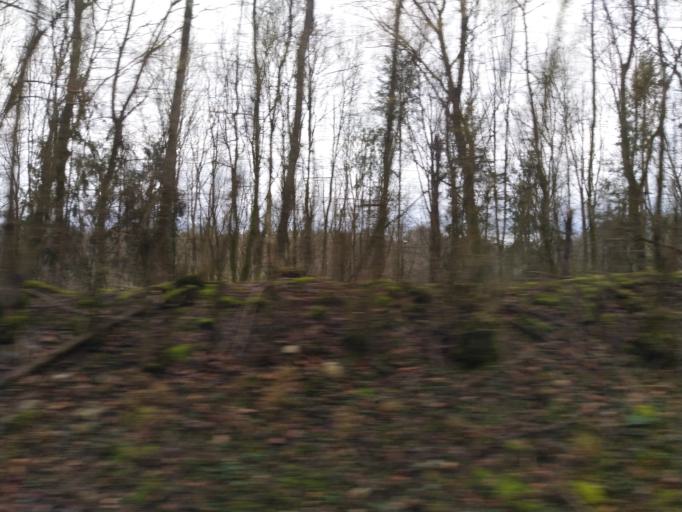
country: DE
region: Baden-Wuerttemberg
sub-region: Regierungsbezirk Stuttgart
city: Mittelschontal
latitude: 48.9334
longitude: 9.3940
